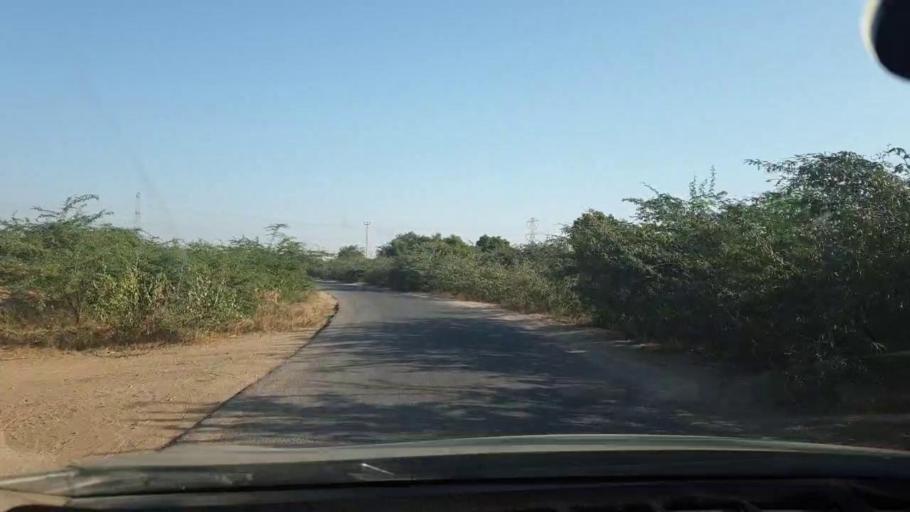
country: PK
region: Sindh
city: Malir Cantonment
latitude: 25.1569
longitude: 67.1924
